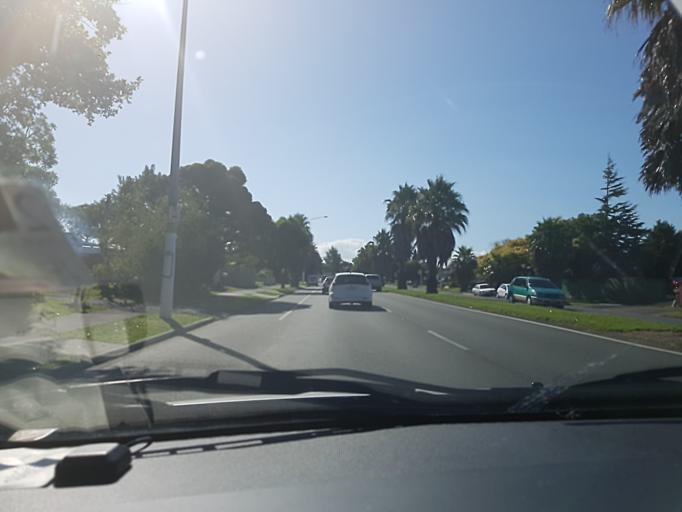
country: NZ
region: Auckland
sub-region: Auckland
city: Tamaki
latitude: -36.9196
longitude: 174.8762
